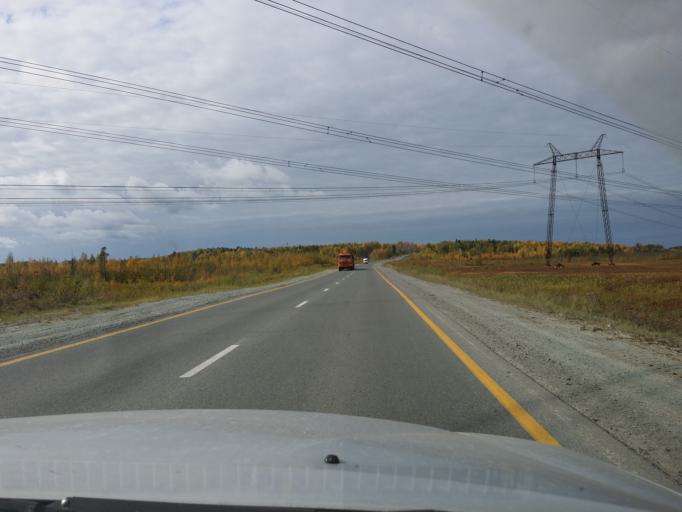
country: RU
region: Khanty-Mansiyskiy Avtonomnyy Okrug
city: Megion
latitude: 61.1073
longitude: 76.0093
